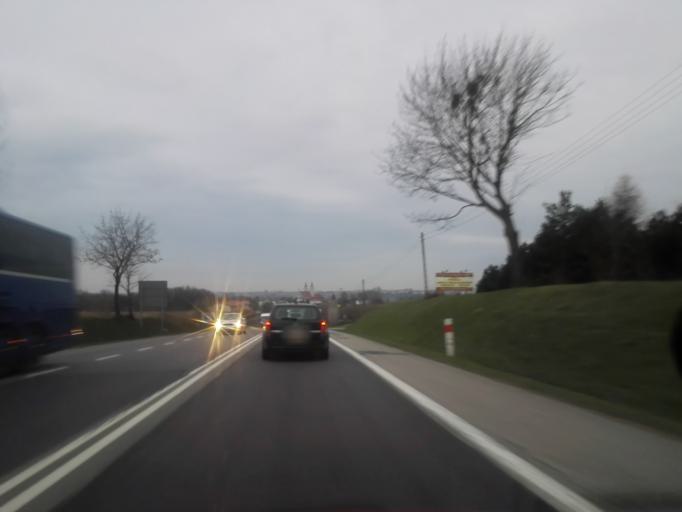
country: PL
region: Podlasie
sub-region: Powiat lomzynski
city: Piatnica
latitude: 53.2052
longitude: 22.1018
